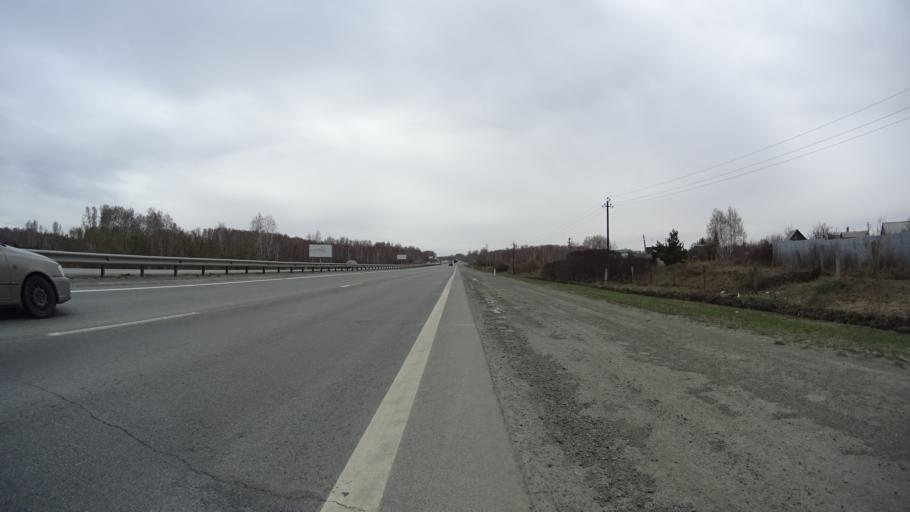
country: RU
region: Chelyabinsk
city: Novosineglazovskiy
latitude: 54.9780
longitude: 61.4117
